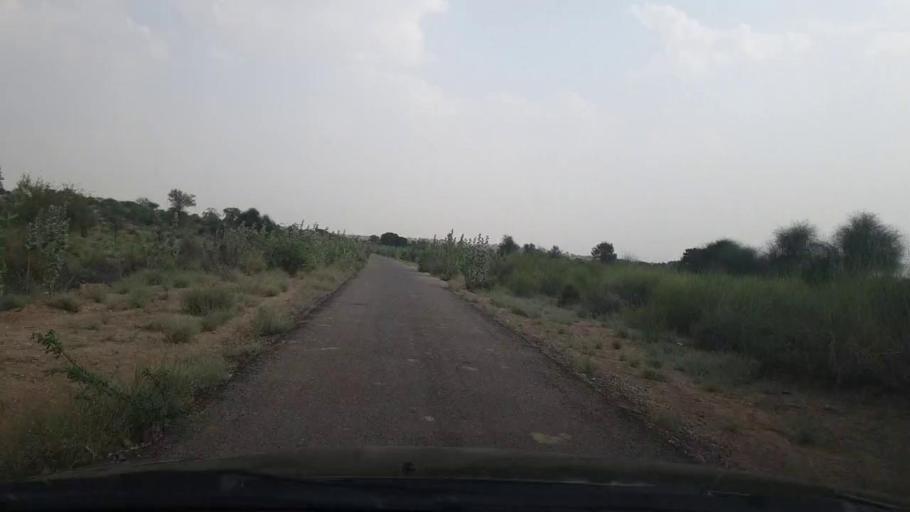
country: PK
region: Sindh
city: Islamkot
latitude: 25.0068
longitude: 70.5977
